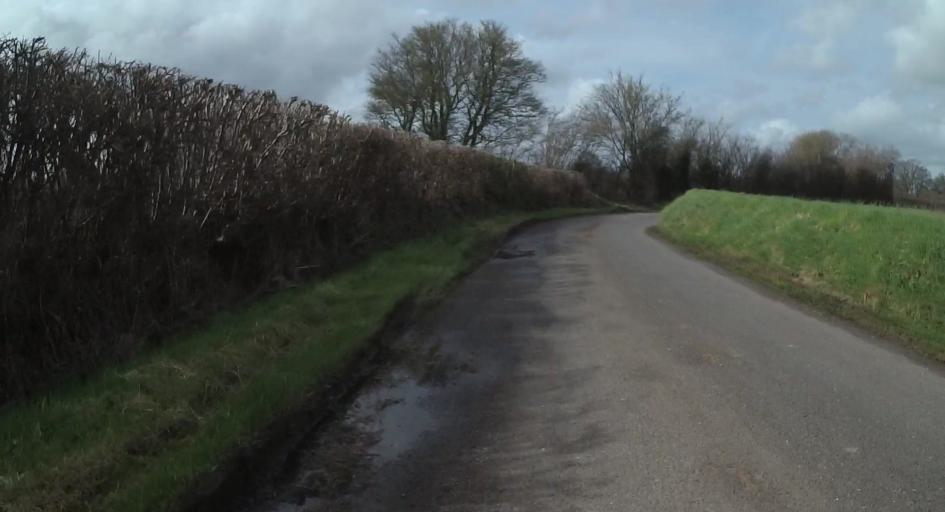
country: GB
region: England
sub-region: Hampshire
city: Kingsclere
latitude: 51.3344
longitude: -1.2456
